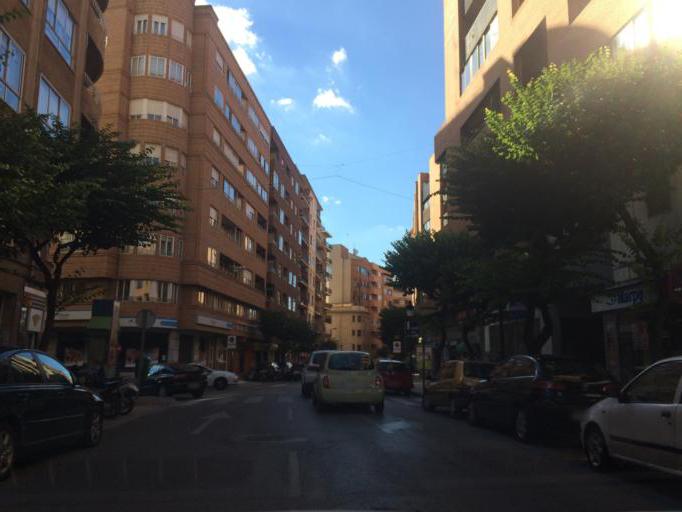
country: ES
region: Castille-La Mancha
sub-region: Provincia de Albacete
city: Albacete
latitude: 38.9933
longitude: -1.8580
